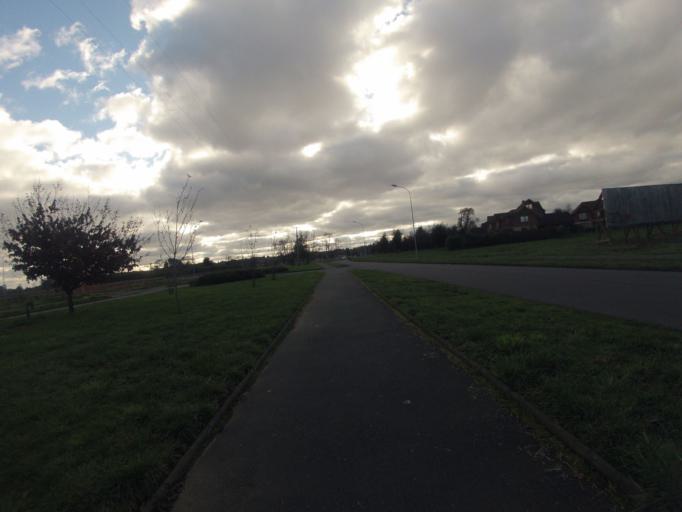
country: CL
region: Araucania
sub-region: Provincia de Cautin
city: Temuco
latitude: -38.7470
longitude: -72.6472
